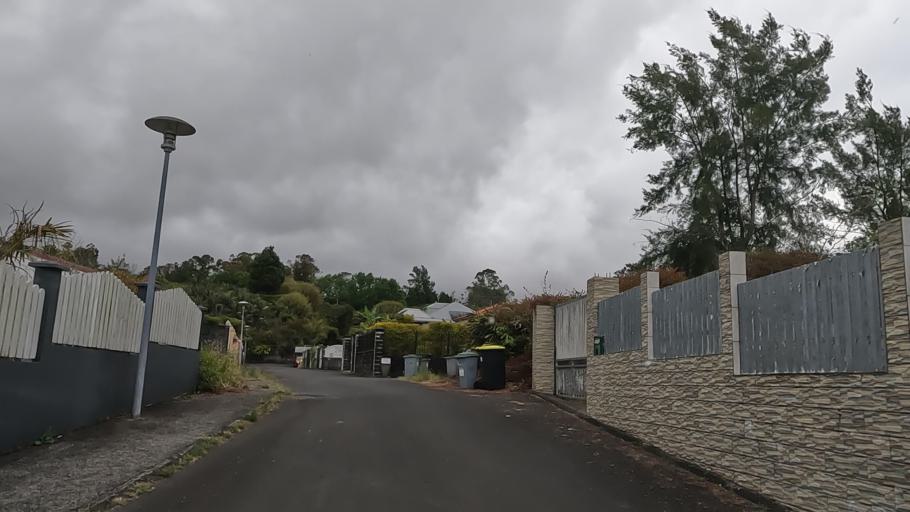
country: RE
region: Reunion
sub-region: Reunion
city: Saint-Benoit
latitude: -21.1402
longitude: 55.6260
